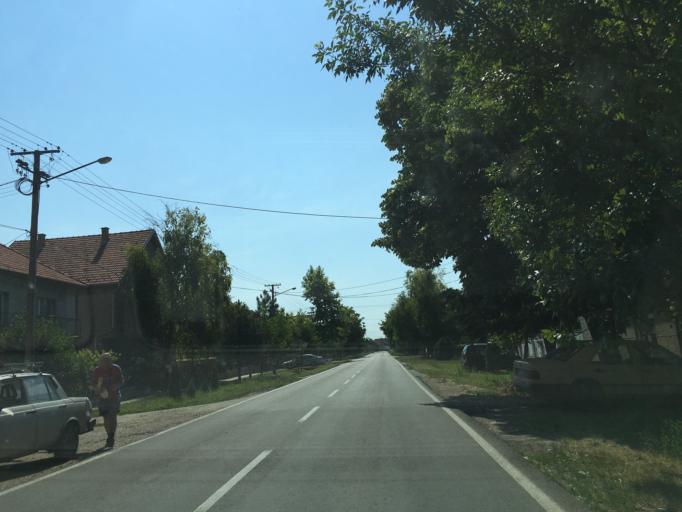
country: RS
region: Autonomna Pokrajina Vojvodina
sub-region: Juznobanatski Okrug
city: Pancevo
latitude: 44.8042
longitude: 20.7116
